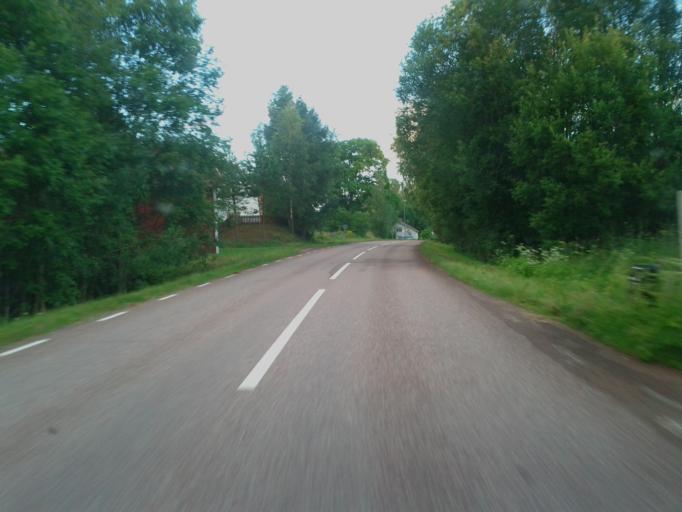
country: SE
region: Dalarna
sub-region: Borlange Kommun
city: Borlaenge
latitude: 60.3417
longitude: 15.4046
